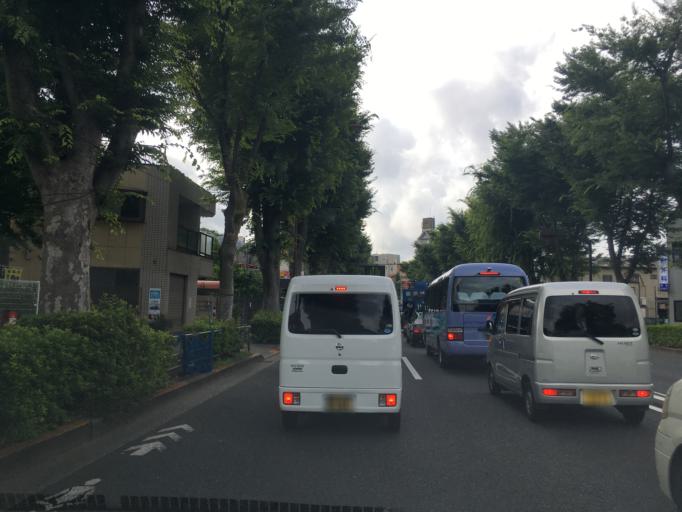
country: JP
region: Tokyo
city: Musashino
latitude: 35.7192
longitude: 139.5927
